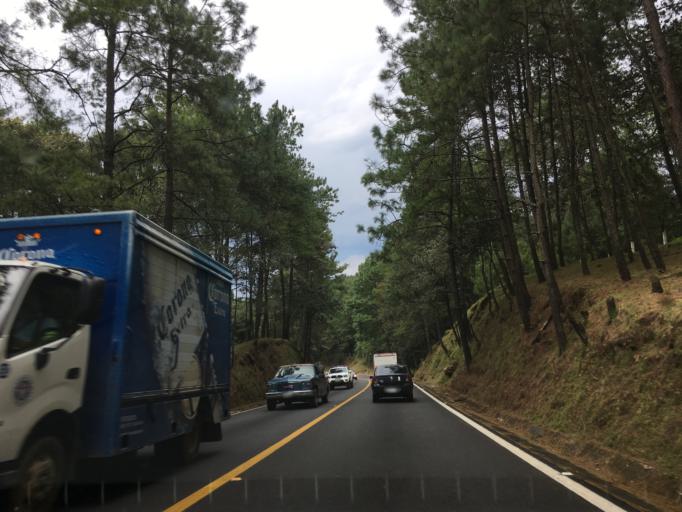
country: MX
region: Michoacan
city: Tingambato
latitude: 19.5017
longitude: -101.8314
